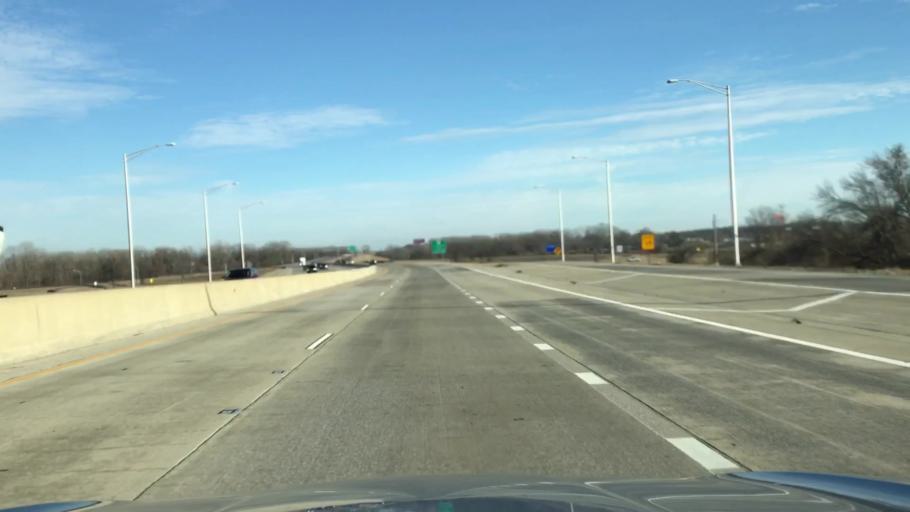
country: US
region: Illinois
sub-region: Madison County
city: Mitchell
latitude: 38.7660
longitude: -90.1286
